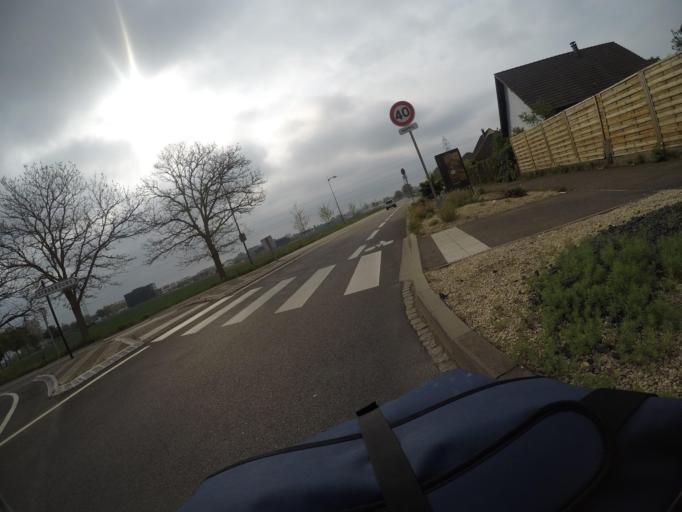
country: FR
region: Alsace
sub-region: Departement du Bas-Rhin
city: Mittelhausbergen
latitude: 48.6119
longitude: 7.6975
